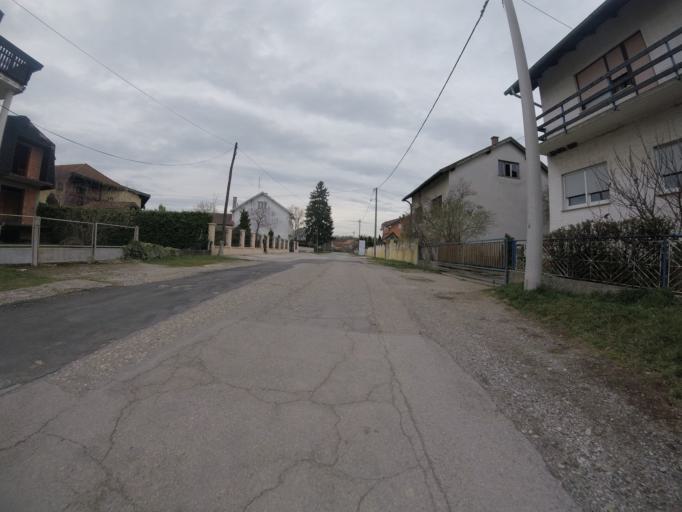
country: HR
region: Zagrebacka
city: Lukavec
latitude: 45.7011
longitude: 15.9895
